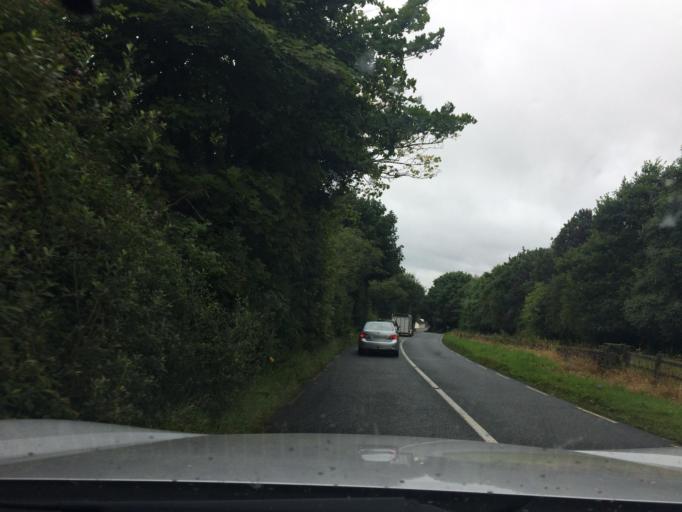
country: IE
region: Munster
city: Cashel
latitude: 52.4734
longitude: -7.8406
